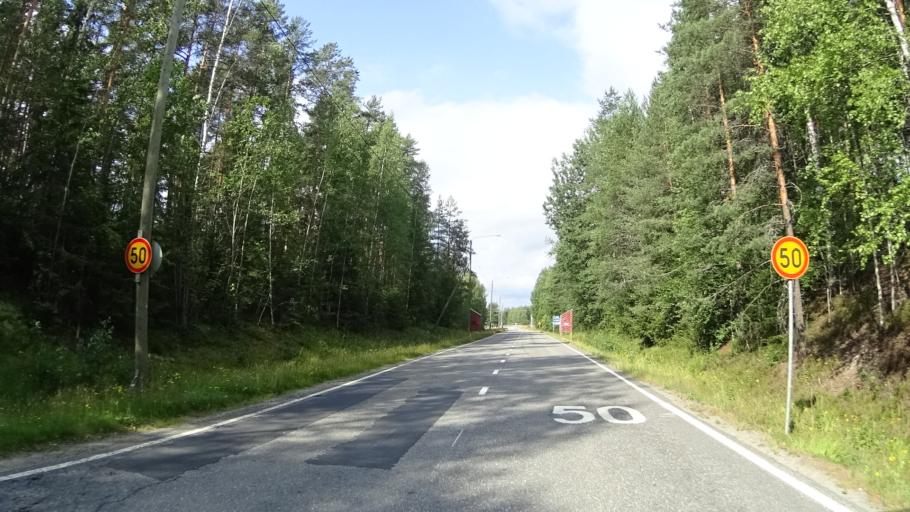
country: FI
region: Pirkanmaa
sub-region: Tampere
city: Luopioinen
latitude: 61.4826
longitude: 24.7154
